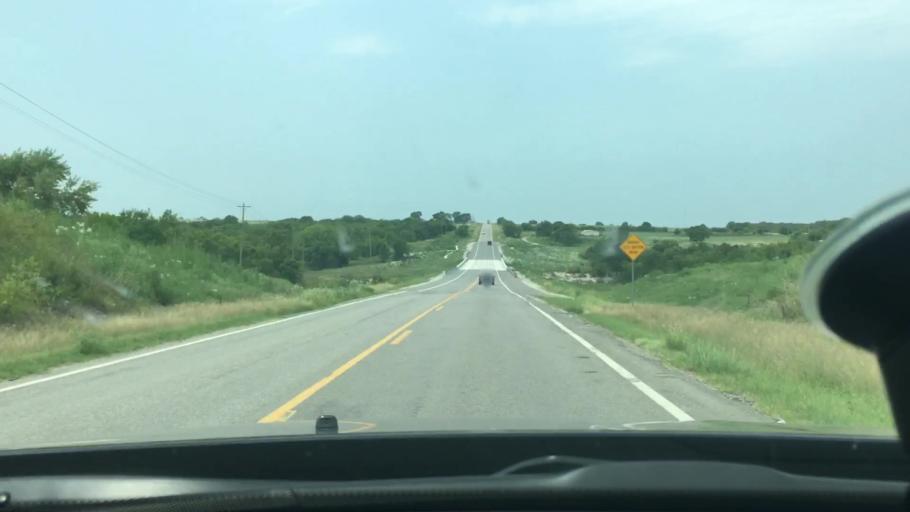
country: US
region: Oklahoma
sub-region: Marshall County
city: Kingston
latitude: 33.9983
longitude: -96.7799
